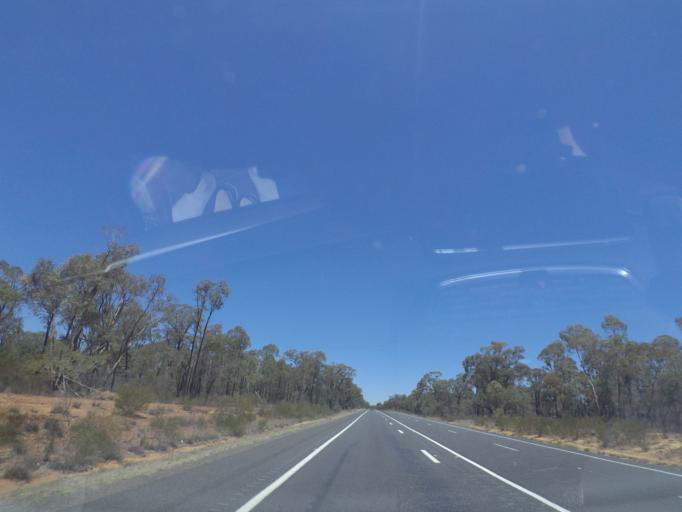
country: AU
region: New South Wales
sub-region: Warrumbungle Shire
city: Coonabarabran
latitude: -30.8736
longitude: 149.4492
